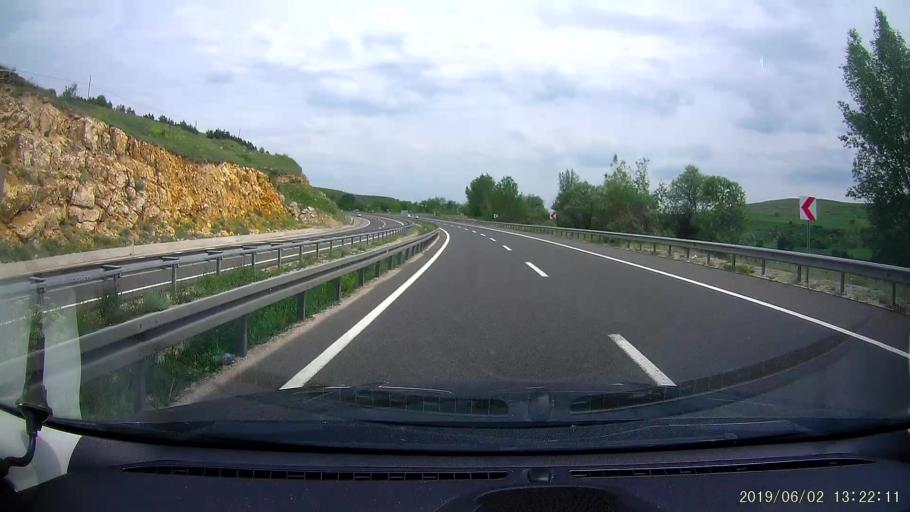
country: TR
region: Cankiri
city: Cerkes
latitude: 40.8258
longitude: 32.7921
